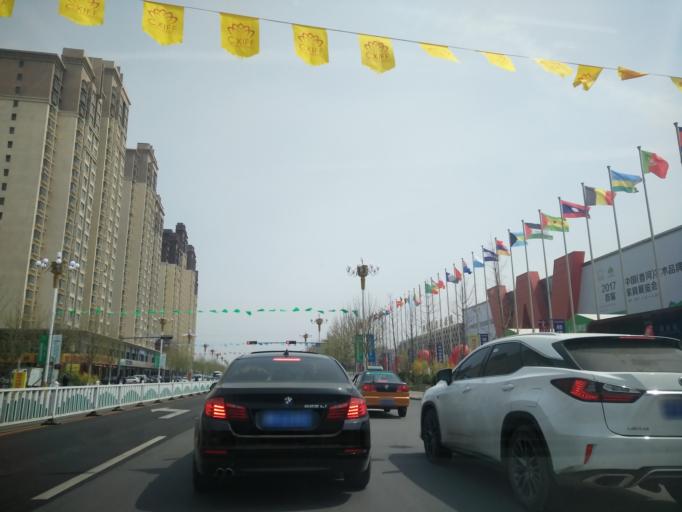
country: CN
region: Beijing
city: Xiji
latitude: 39.7467
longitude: 116.9958
